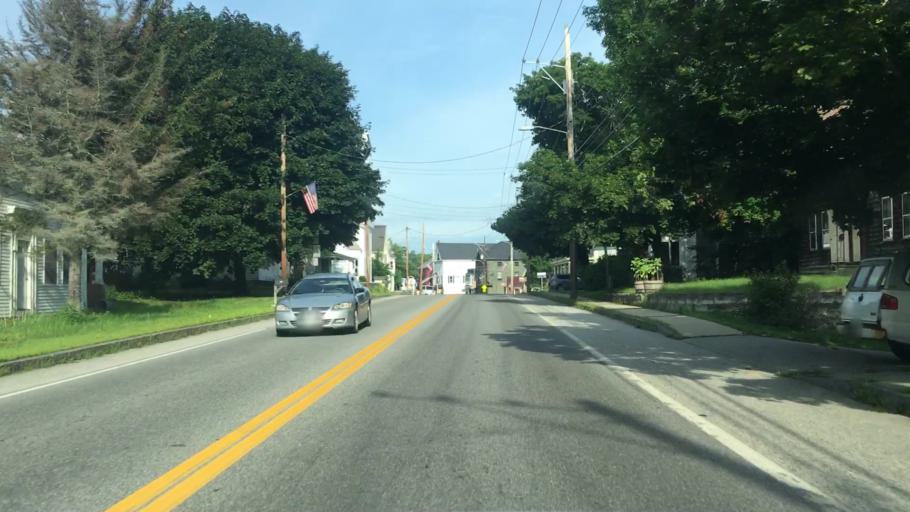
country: US
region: Maine
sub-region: York County
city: Cornish
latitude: 43.8047
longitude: -70.7995
